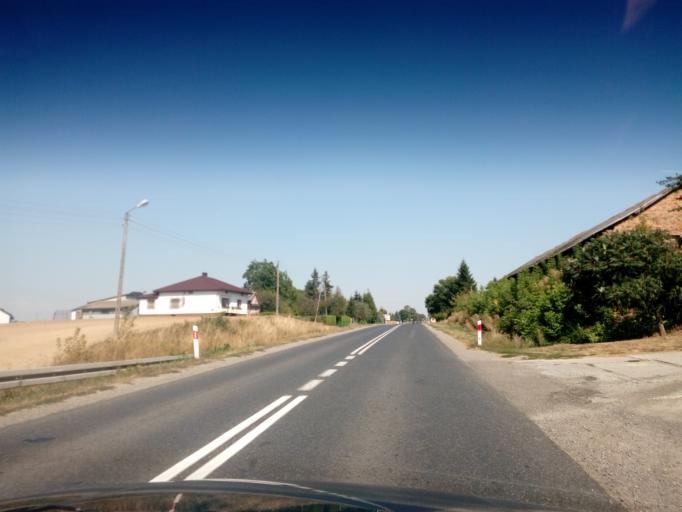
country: PL
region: Lublin Voivodeship
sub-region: Powiat hrubieszowski
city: Hrubieszow
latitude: 50.8209
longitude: 23.9382
